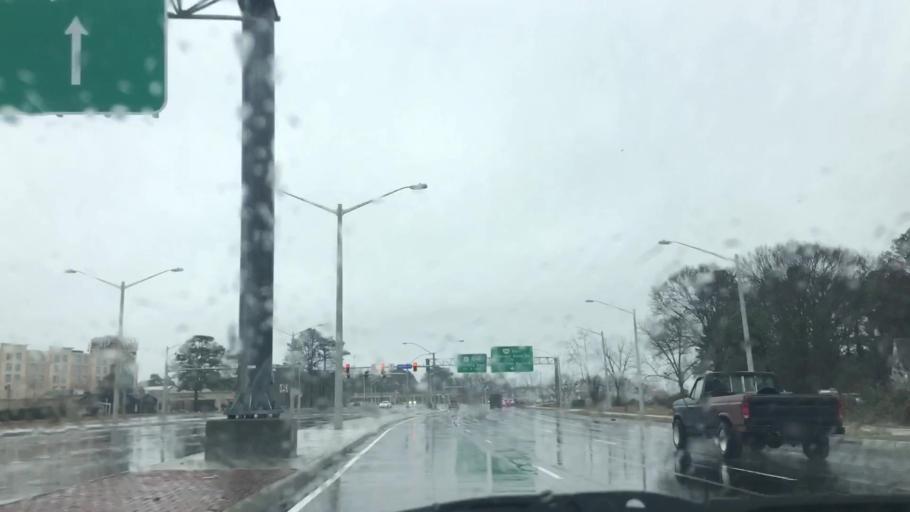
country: US
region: Virginia
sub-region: City of Norfolk
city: Norfolk
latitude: 36.8776
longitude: -76.2114
